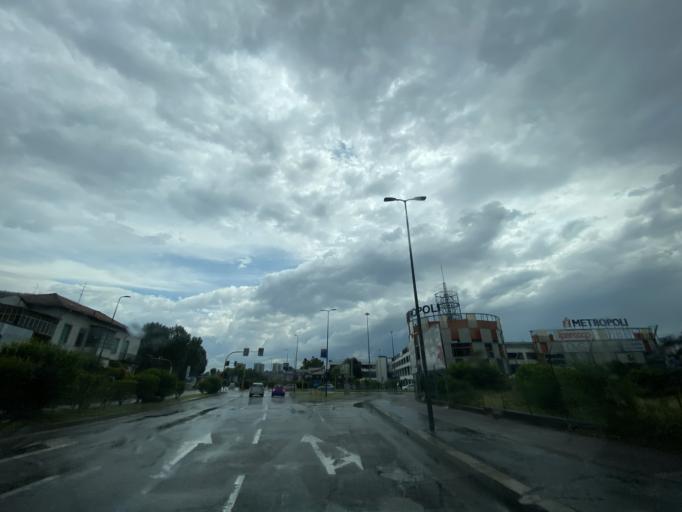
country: IT
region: Lombardy
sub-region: Citta metropolitana di Milano
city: Novate Milanese
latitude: 45.5216
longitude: 9.1505
